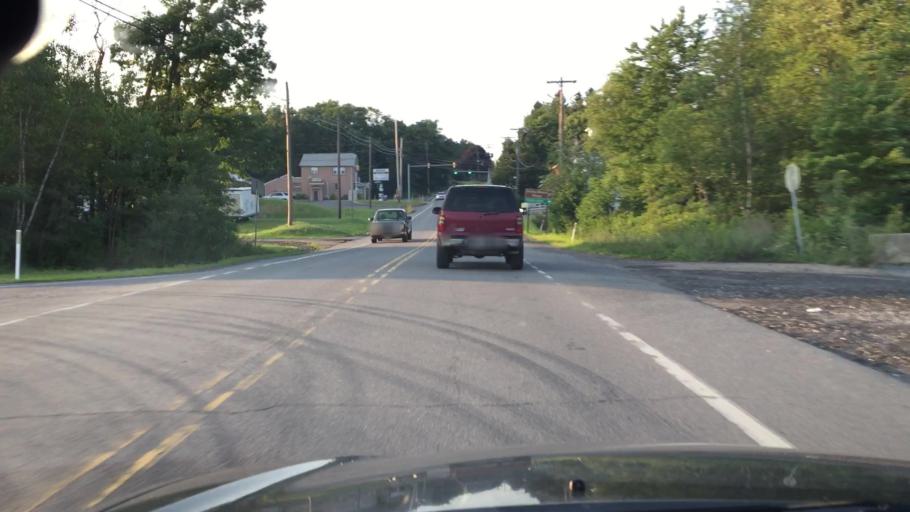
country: US
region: Pennsylvania
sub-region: Luzerne County
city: Harleigh
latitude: 40.9792
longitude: -75.9757
